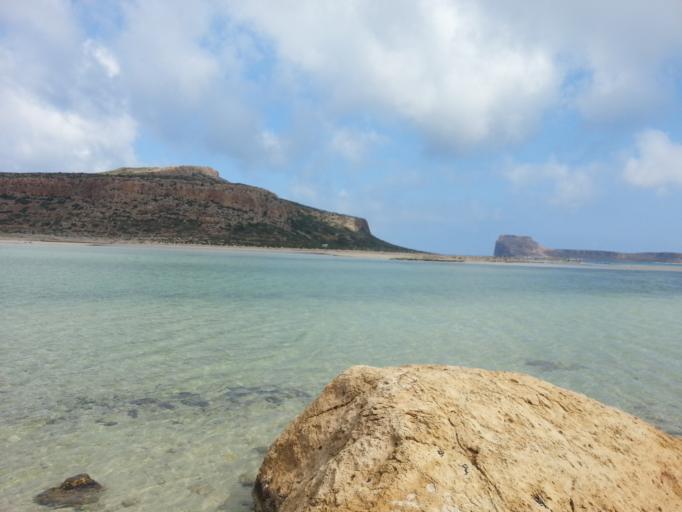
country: GR
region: Crete
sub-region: Nomos Chanias
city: Kissamos
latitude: 35.5814
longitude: 23.5908
